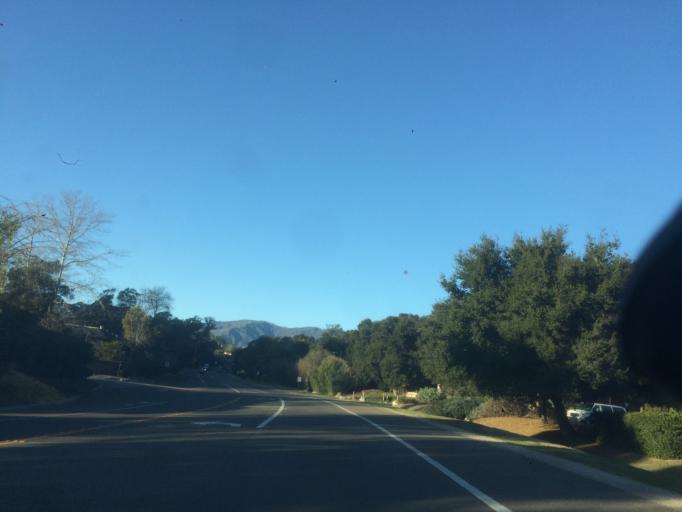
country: US
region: California
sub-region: Santa Barbara County
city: Santa Barbara
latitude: 34.4142
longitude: -119.7401
